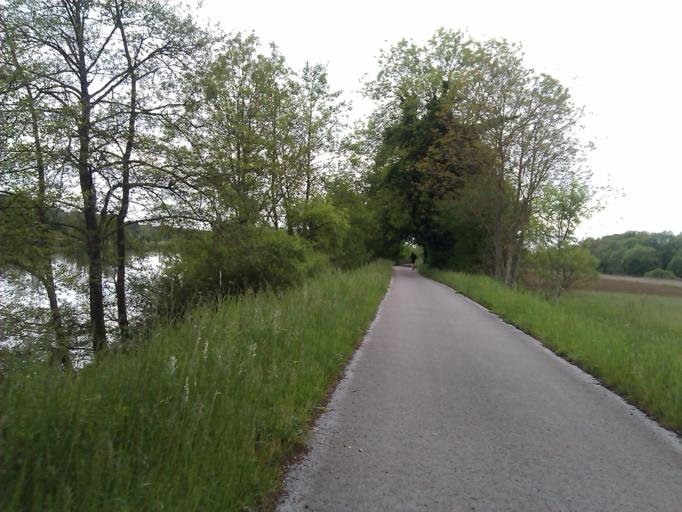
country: FR
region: Franche-Comte
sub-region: Departement du Jura
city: Fraisans
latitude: 47.1629
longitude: 5.7763
